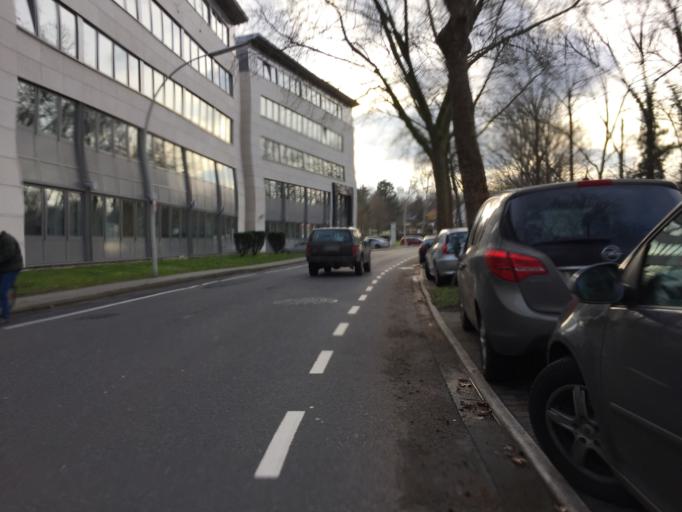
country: DE
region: North Rhine-Westphalia
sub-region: Regierungsbezirk Koln
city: Bonn
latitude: 50.7346
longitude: 7.0707
